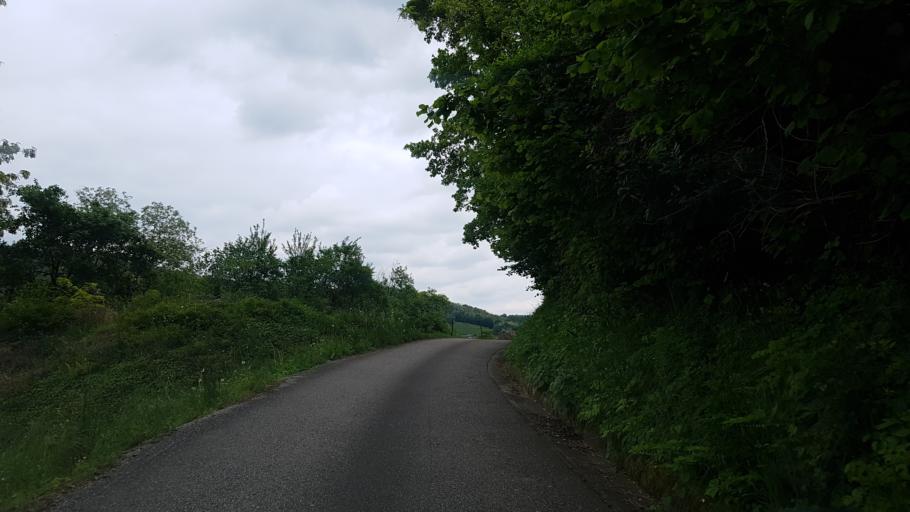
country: IT
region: Friuli Venezia Giulia
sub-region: Provincia di Udine
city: Cividale del Friuli
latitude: 46.0805
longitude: 13.4478
